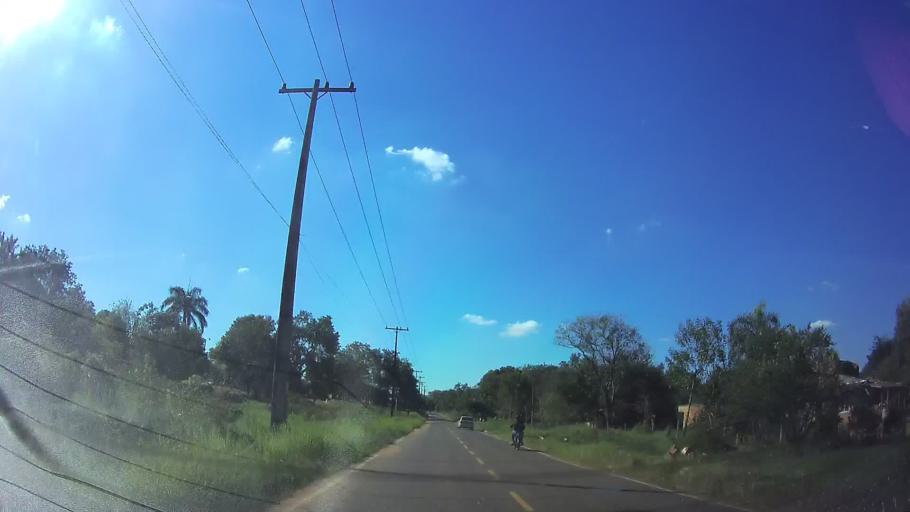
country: PY
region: Central
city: Limpio
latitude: -25.1909
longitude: -57.4754
